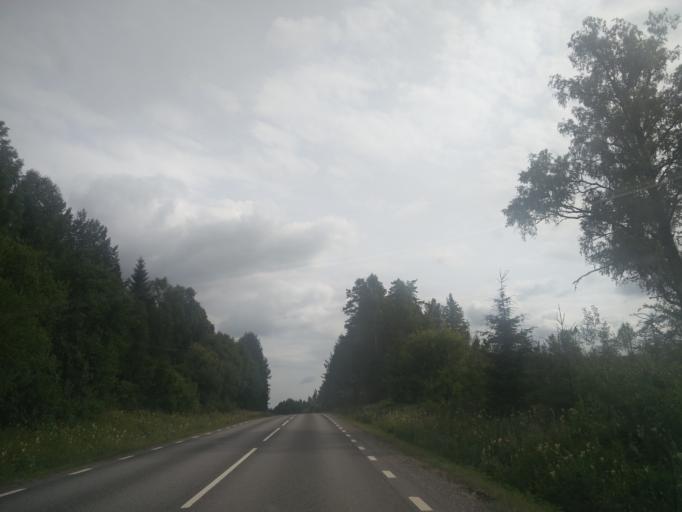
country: SE
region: Vaermland
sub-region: Arvika Kommun
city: Arvika
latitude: 59.7283
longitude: 12.5655
